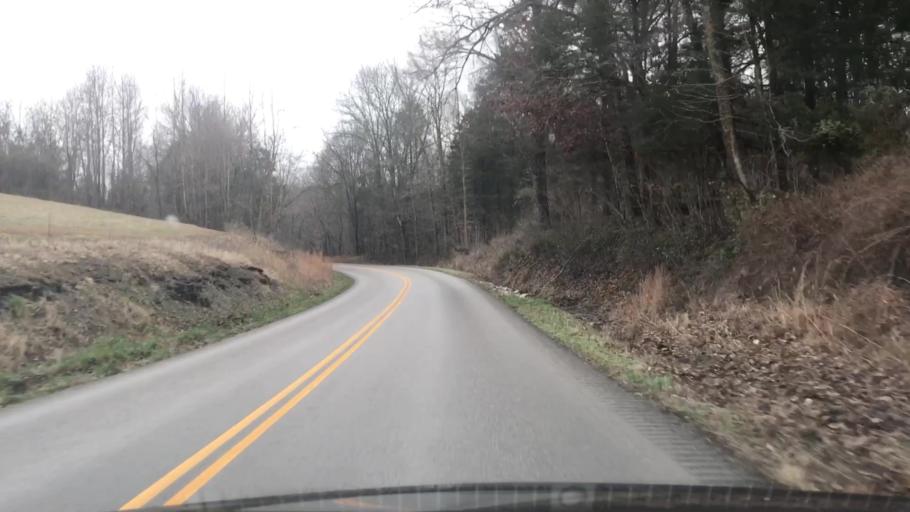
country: US
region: Kentucky
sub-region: Barren County
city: Glasgow
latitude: 36.8877
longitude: -85.7901
